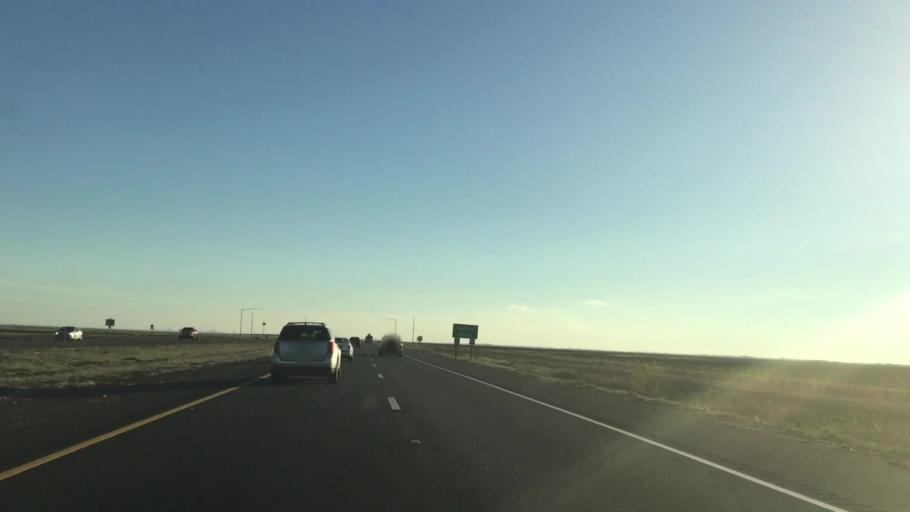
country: US
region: California
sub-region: Sacramento County
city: Elverta
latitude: 38.7829
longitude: -121.5436
